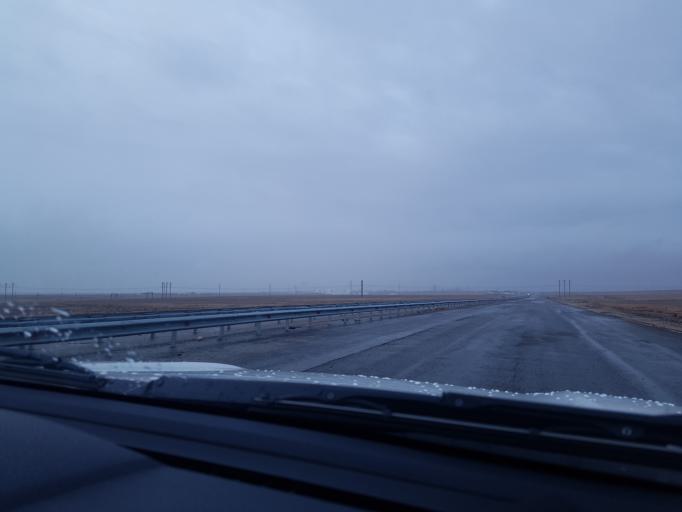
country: TM
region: Balkan
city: Balkanabat
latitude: 39.9232
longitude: 53.8729
